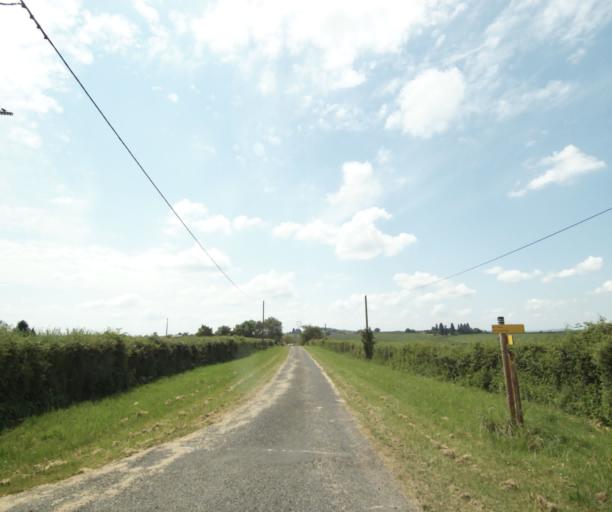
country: FR
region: Bourgogne
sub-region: Departement de Saone-et-Loire
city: Perrecy-les-Forges
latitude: 46.6002
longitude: 4.1436
